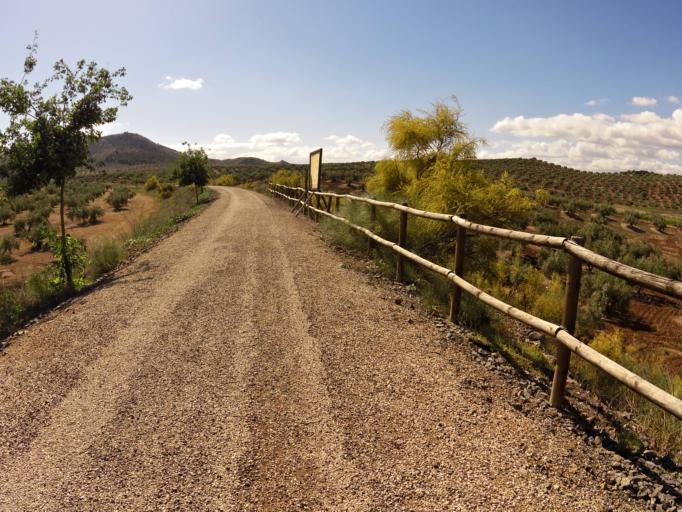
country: ES
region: Andalusia
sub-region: Provincia de Jaen
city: Alcaudete
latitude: 37.6015
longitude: -4.1426
